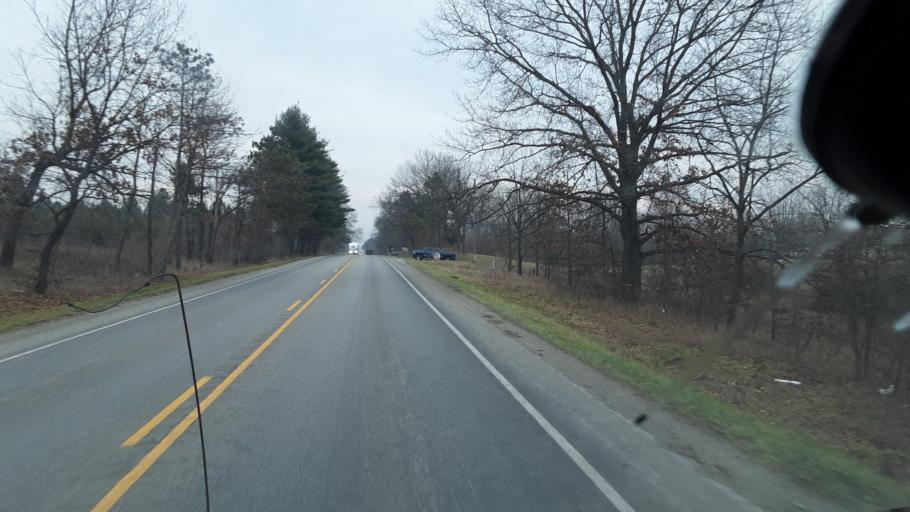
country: US
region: Indiana
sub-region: Elkhart County
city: Middlebury
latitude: 41.7258
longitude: -85.6786
